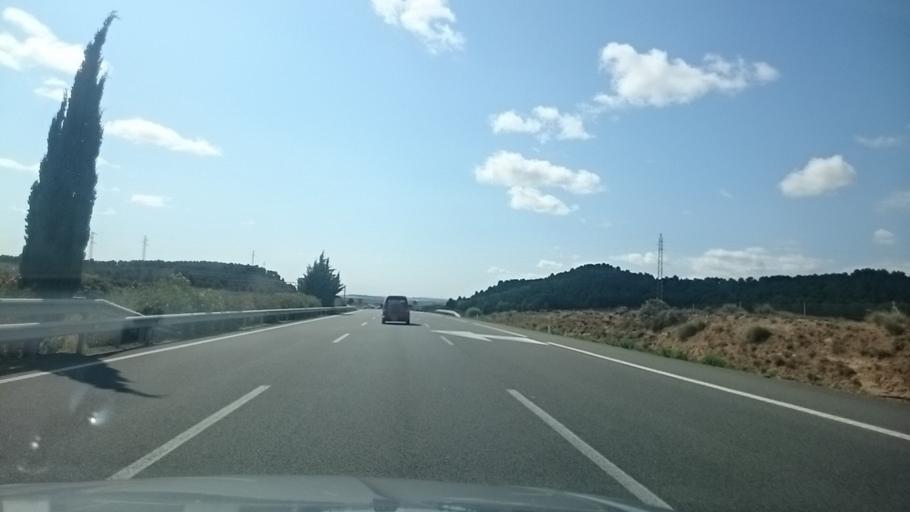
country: ES
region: Navarre
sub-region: Provincia de Navarra
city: Murchante
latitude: 42.0852
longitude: -1.7131
